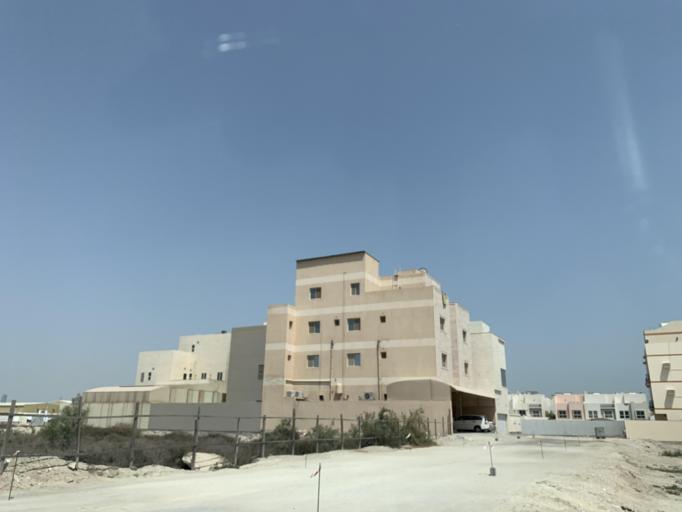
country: BH
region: Northern
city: Madinat `Isa
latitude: 26.1898
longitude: 50.5424
